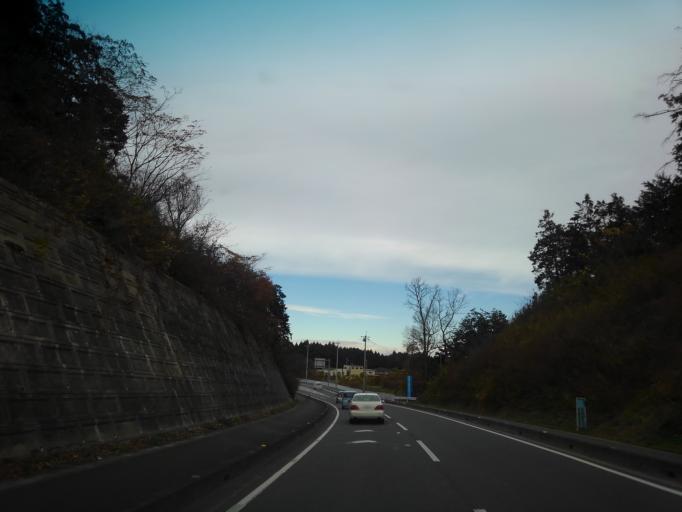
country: JP
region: Saitama
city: Morohongo
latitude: 35.9246
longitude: 139.3211
